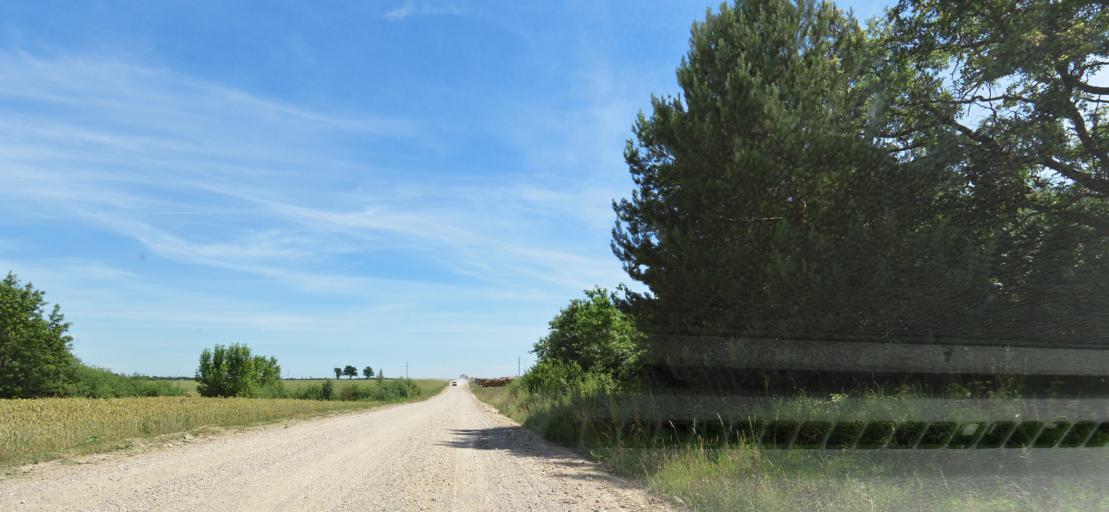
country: LT
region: Vilnius County
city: Ukmerge
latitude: 55.3023
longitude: 24.8036
